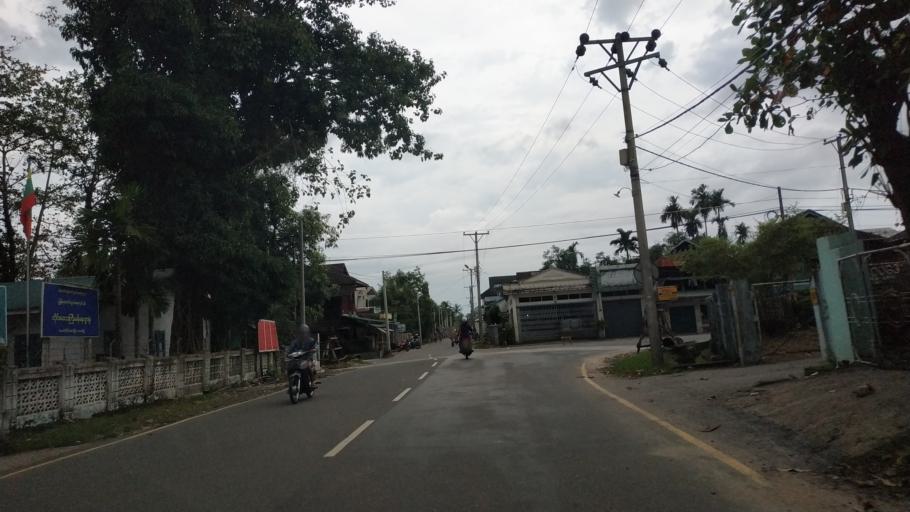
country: MM
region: Tanintharyi
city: Dawei
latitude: 14.0723
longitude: 98.1939
